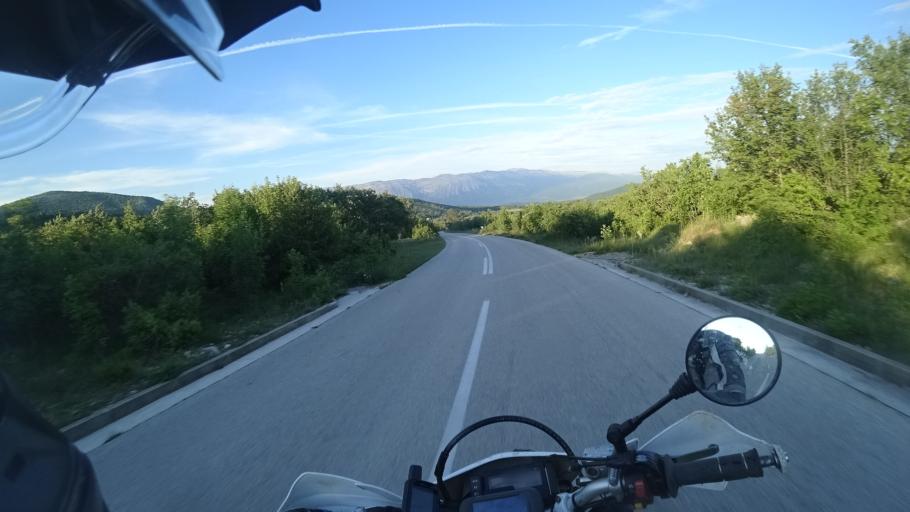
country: HR
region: Sibensko-Kniniska
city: Drnis
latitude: 43.8930
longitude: 16.3580
